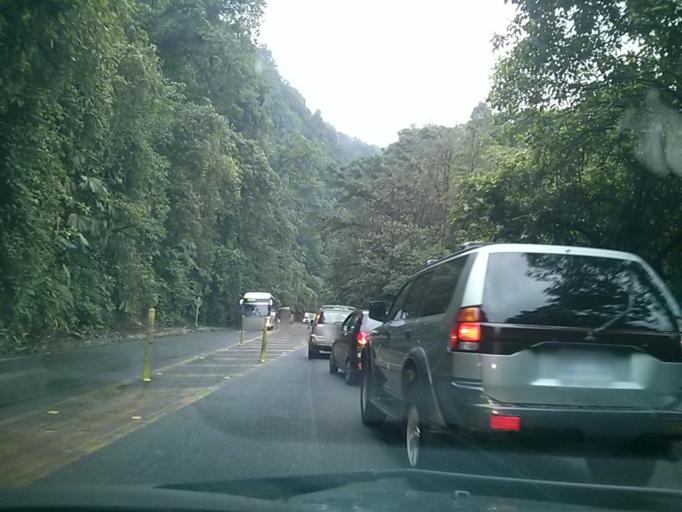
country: CR
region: San Jose
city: Dulce Nombre de Jesus
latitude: 10.1008
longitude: -83.9771
